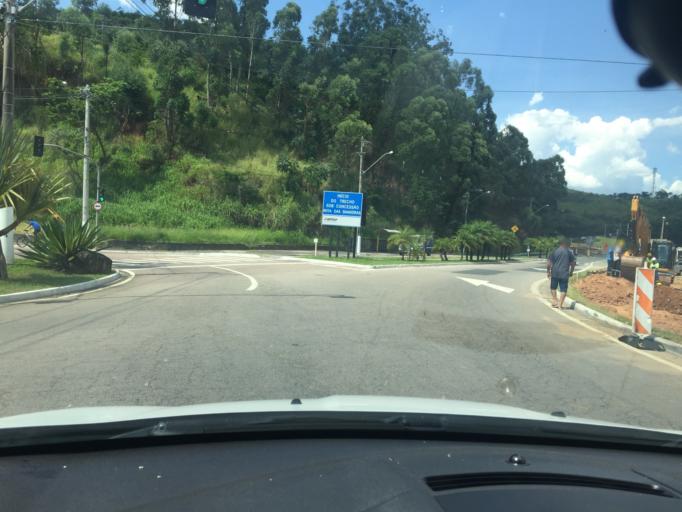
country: BR
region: Sao Paulo
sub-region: Jundiai
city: Jundiai
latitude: -23.1716
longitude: -46.8848
